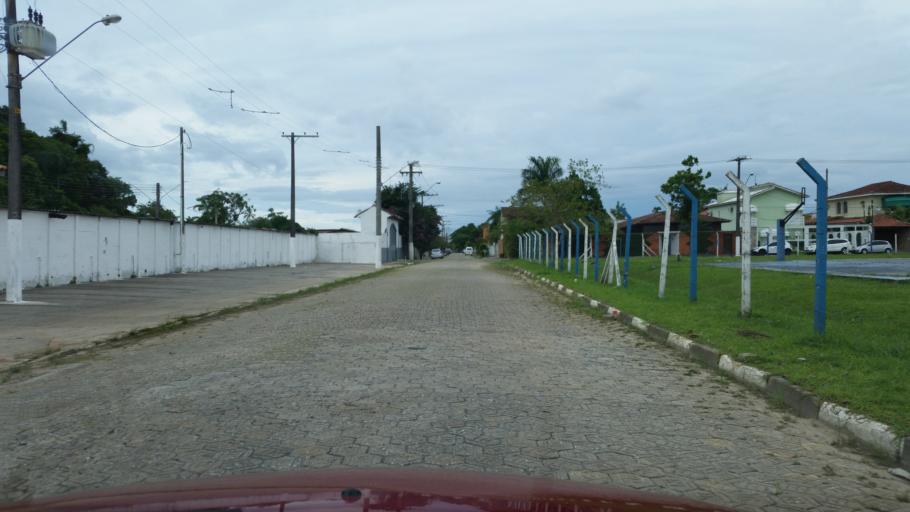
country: BR
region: Sao Paulo
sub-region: Iguape
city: Iguape
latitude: -24.7037
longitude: -47.5531
